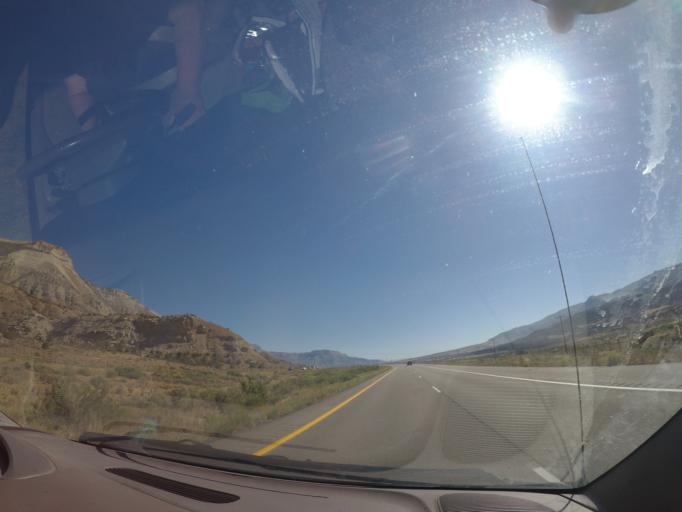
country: US
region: Colorado
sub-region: Garfield County
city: Parachute
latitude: 39.4096
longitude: -108.0981
